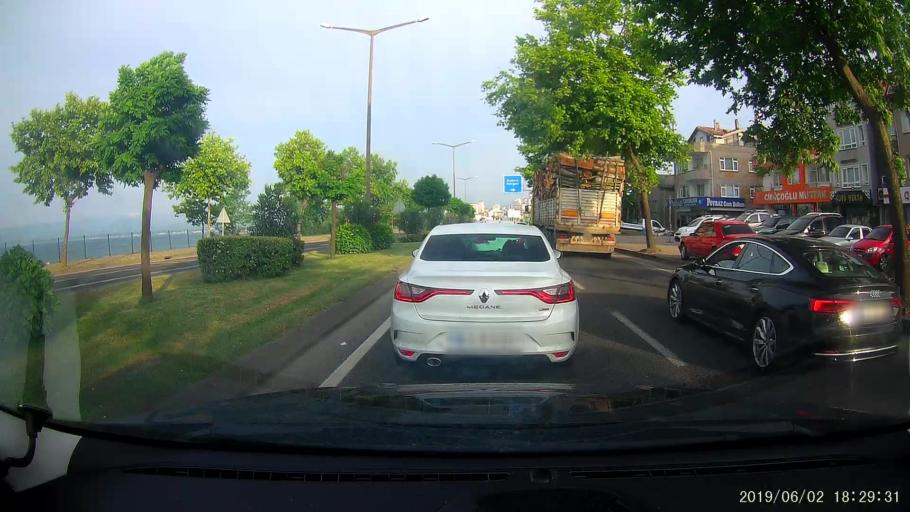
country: TR
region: Ordu
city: Fatsa
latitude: 41.0388
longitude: 37.4906
